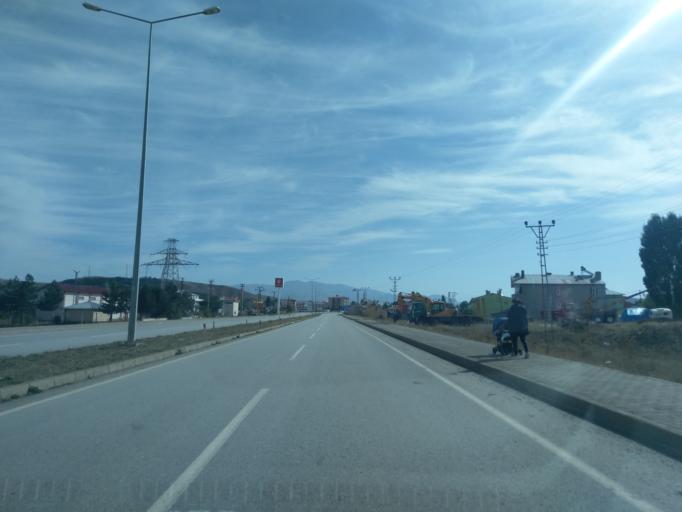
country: TR
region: Sivas
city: Imranli
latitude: 39.8710
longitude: 38.1036
